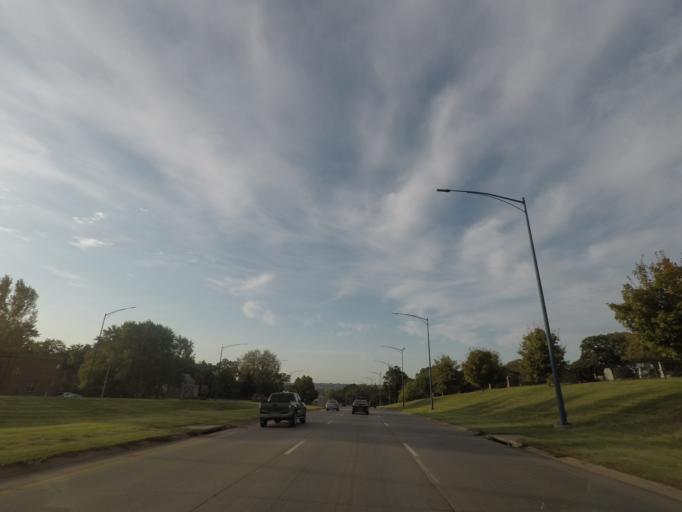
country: US
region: Iowa
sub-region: Polk County
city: Des Moines
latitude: 41.5932
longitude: -93.6445
